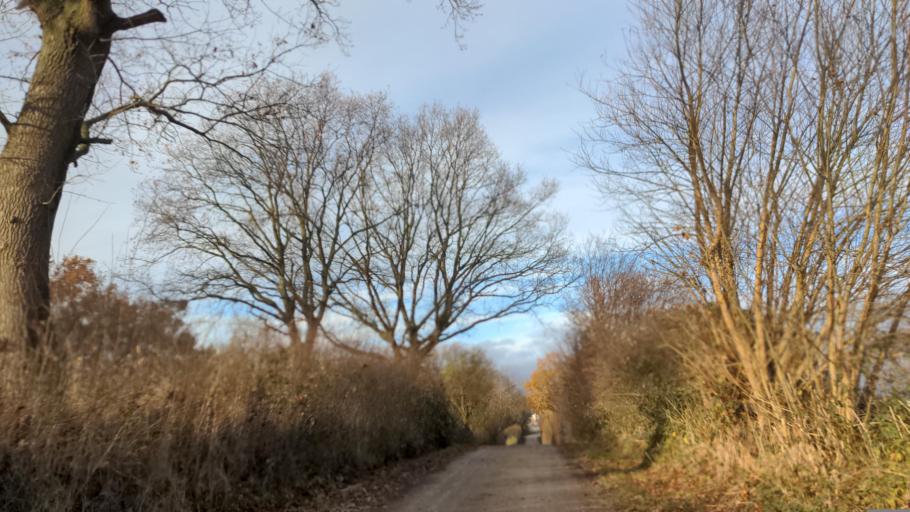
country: DE
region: Schleswig-Holstein
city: Neustadt in Holstein
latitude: 54.0895
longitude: 10.7932
